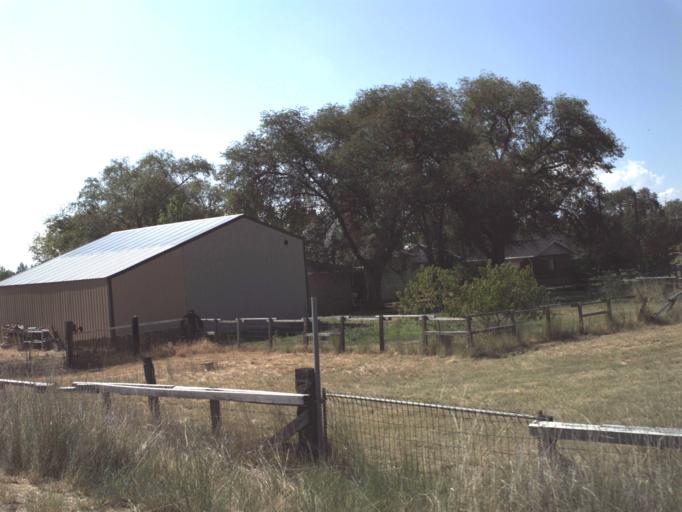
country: US
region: Utah
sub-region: Weber County
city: West Haven
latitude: 41.2444
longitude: -112.0788
